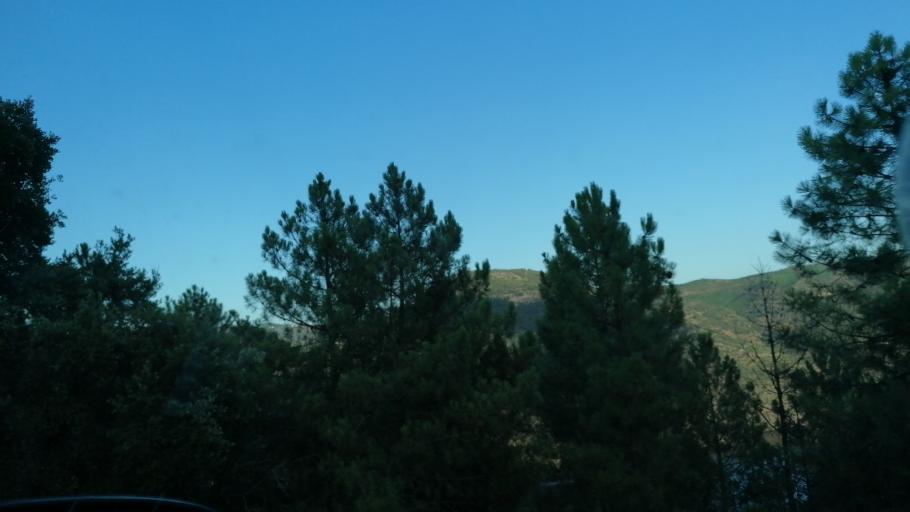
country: PT
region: Viseu
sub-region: Sao Joao da Pesqueira
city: Sao Joao da Pesqueira
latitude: 41.2451
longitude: -7.4311
